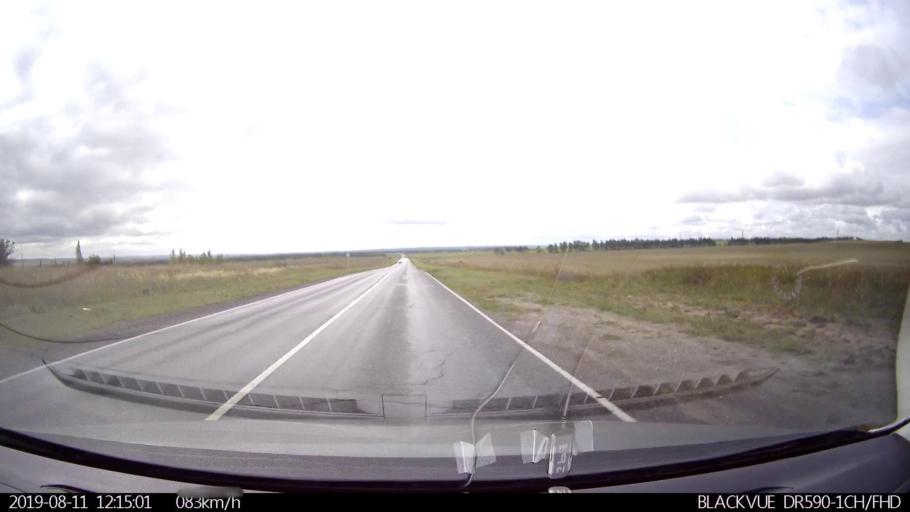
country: RU
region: Ulyanovsk
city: Ignatovka
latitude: 53.9461
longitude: 47.9726
